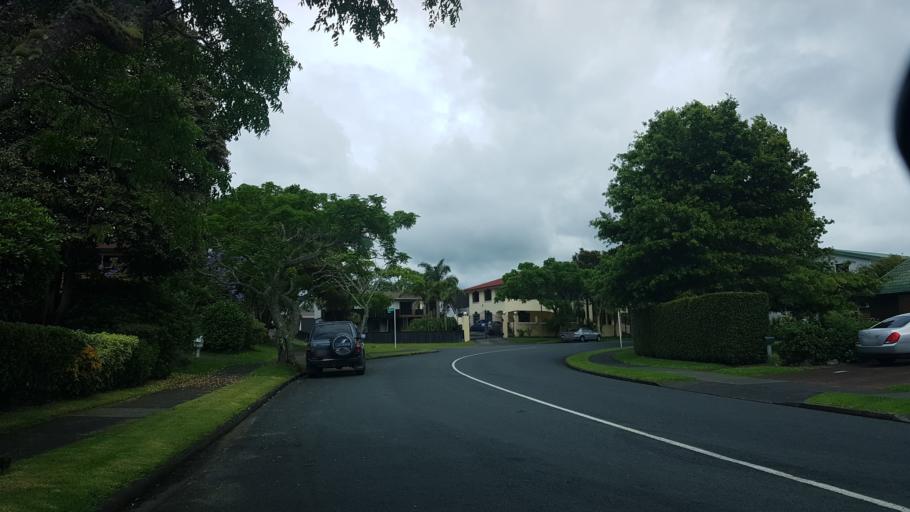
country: NZ
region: Auckland
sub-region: Auckland
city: Rosebank
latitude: -36.8319
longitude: 174.6589
